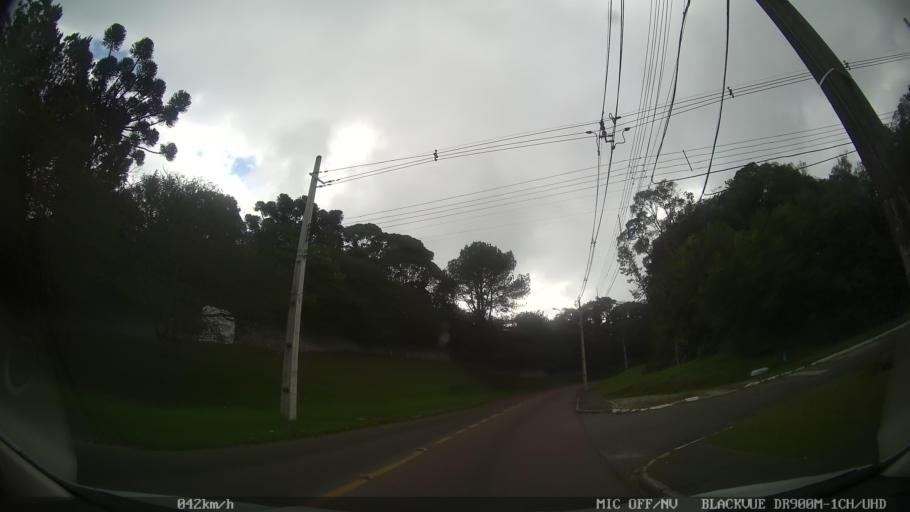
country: BR
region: Parana
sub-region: Almirante Tamandare
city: Almirante Tamandare
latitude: -25.3630
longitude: -49.2547
